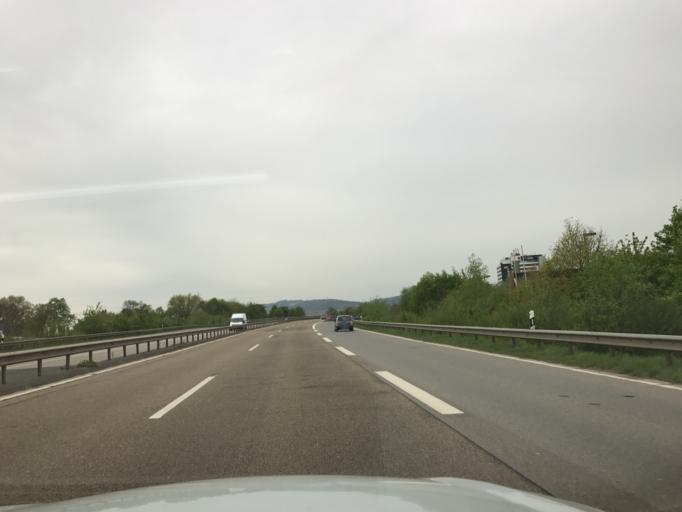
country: DE
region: Rheinland-Pfalz
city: Trier
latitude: 49.7739
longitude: 6.6709
